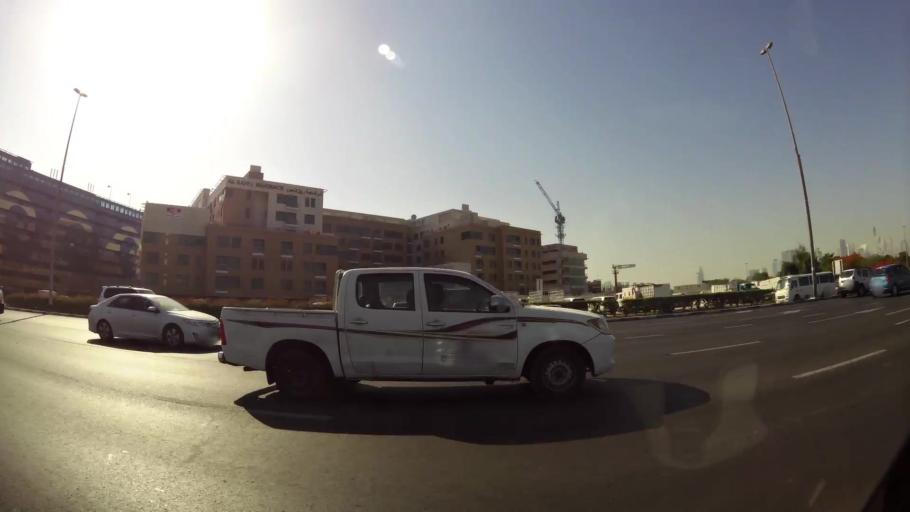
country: AE
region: Ash Shariqah
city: Sharjah
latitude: 25.2510
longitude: 55.2809
